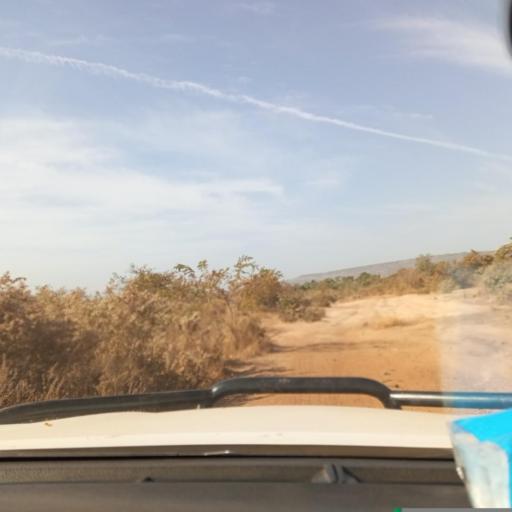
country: ML
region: Bamako
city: Bamako
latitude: 12.5561
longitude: -8.1390
